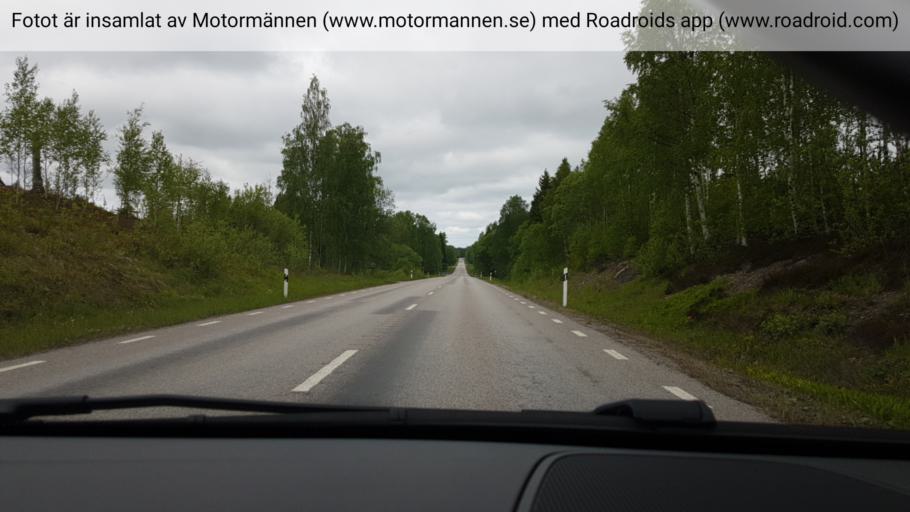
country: SE
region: Uppsala
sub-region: Tierps Kommun
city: Tierp
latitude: 60.3606
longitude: 17.3268
